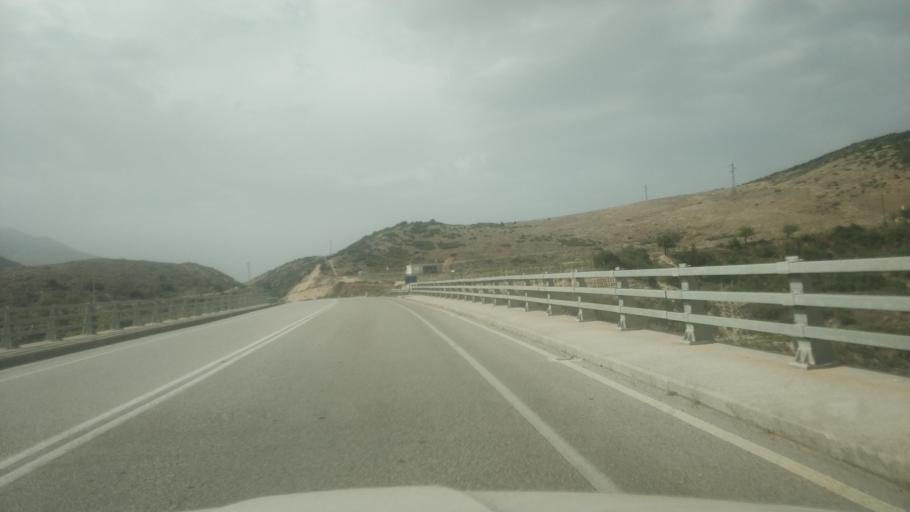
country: AL
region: Gjirokaster
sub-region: Rrethi i Tepelenes
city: Memaliaj
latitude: 40.3634
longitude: 19.9251
